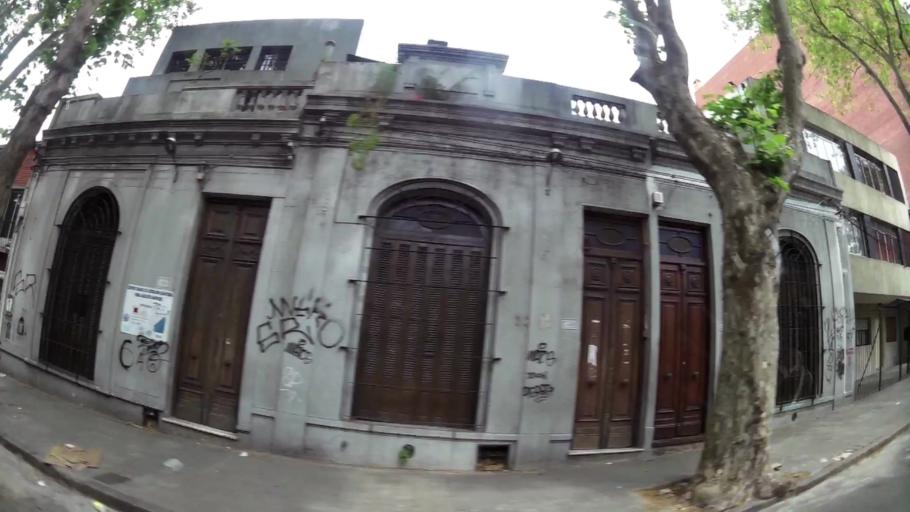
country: UY
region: Montevideo
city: Montevideo
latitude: -34.9032
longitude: -56.1737
